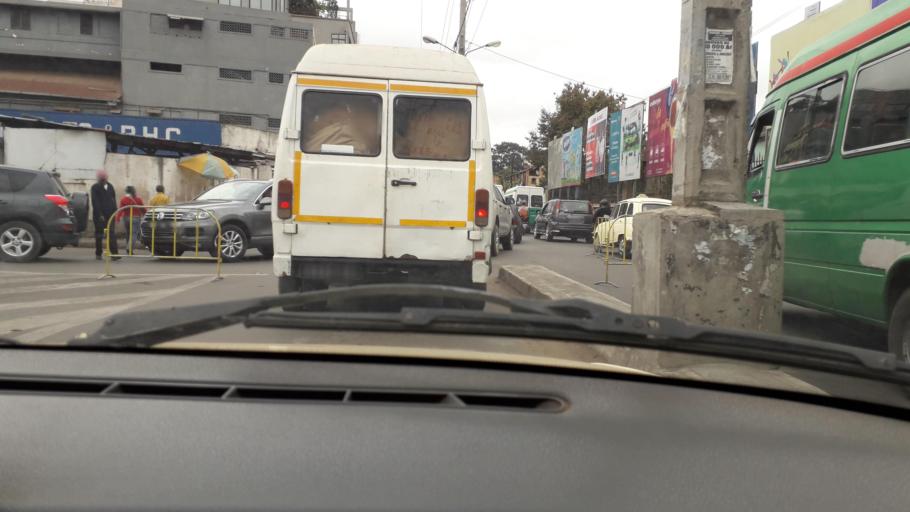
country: MG
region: Analamanga
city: Antananarivo
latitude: -18.9010
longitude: 47.5210
